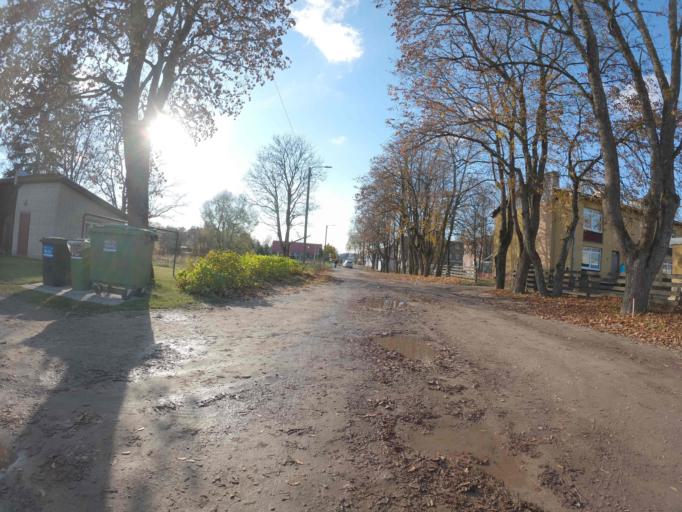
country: EE
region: Raplamaa
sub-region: Rapla vald
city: Rapla
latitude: 59.0051
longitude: 24.7978
